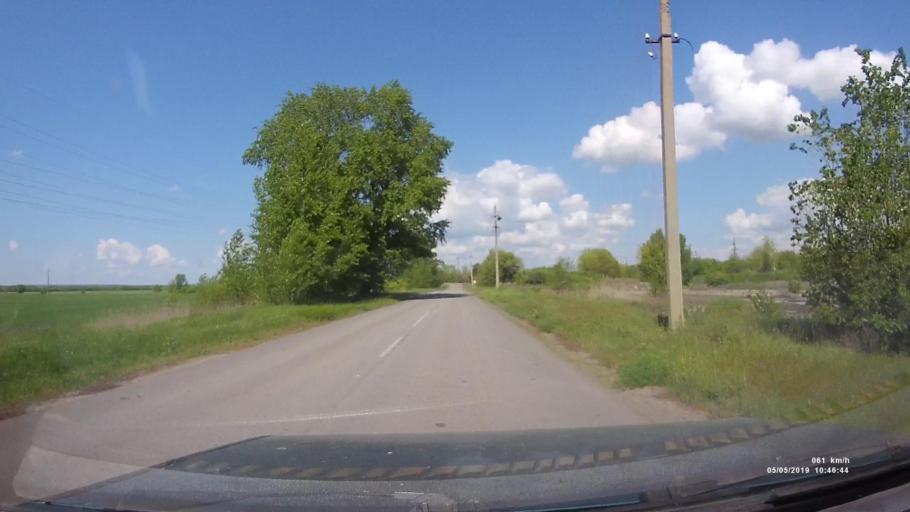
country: RU
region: Rostov
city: Ust'-Donetskiy
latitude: 47.6357
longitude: 40.8414
